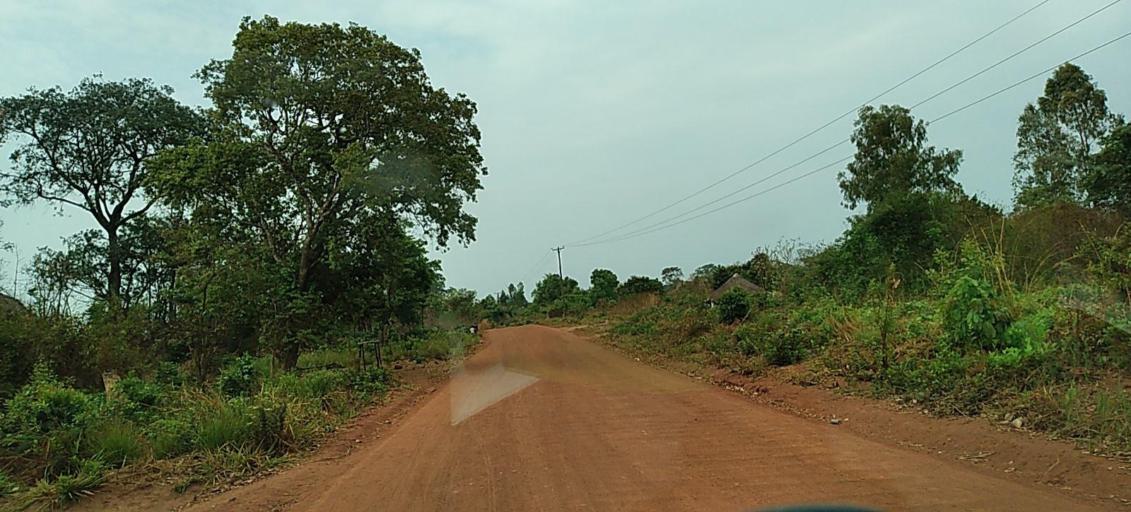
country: ZM
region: North-Western
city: Solwezi
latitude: -12.2421
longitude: 26.5119
